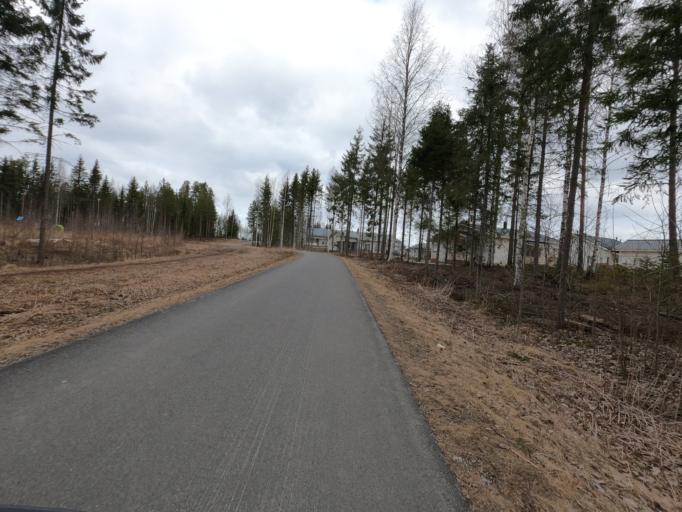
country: FI
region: North Karelia
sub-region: Joensuu
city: Joensuu
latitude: 62.5640
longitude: 29.8210
